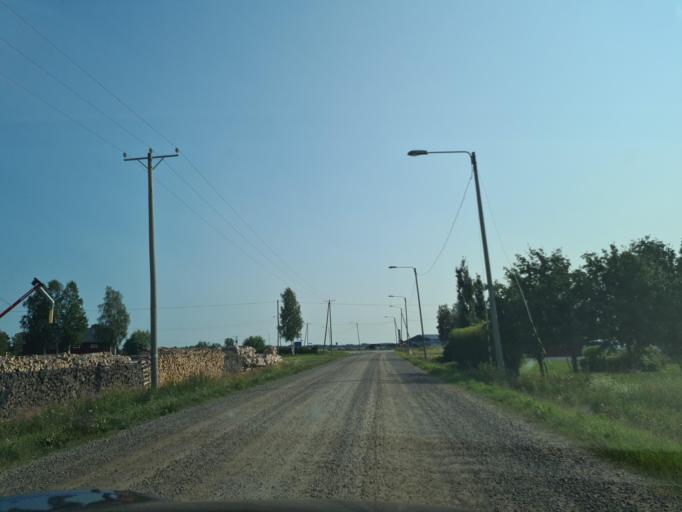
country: FI
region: Ostrobothnia
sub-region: Kyroenmaa
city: Laihia
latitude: 63.0022
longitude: 21.9028
